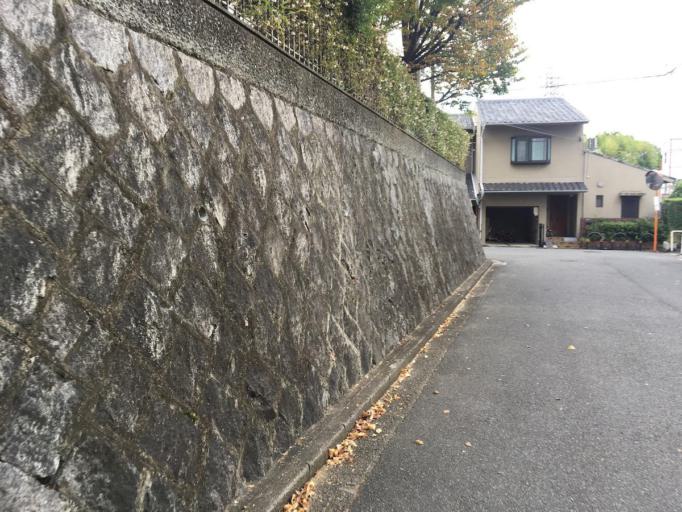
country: JP
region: Osaka
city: Suita
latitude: 34.8030
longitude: 135.5158
